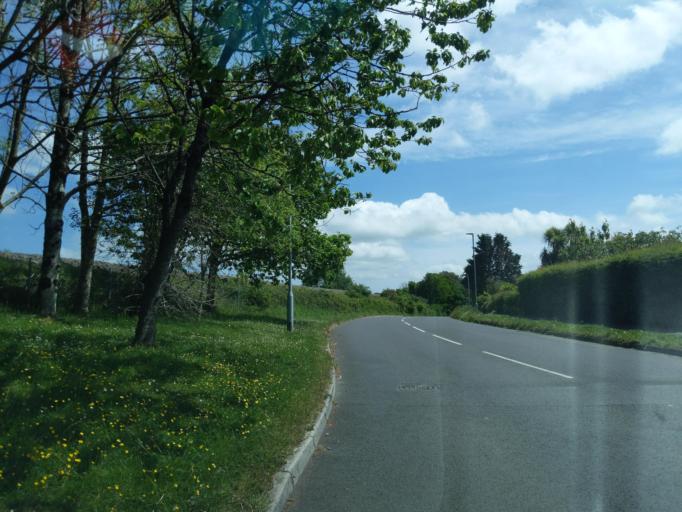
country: GB
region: England
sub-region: Devon
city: Ivybridge
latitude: 50.3943
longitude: -3.9354
